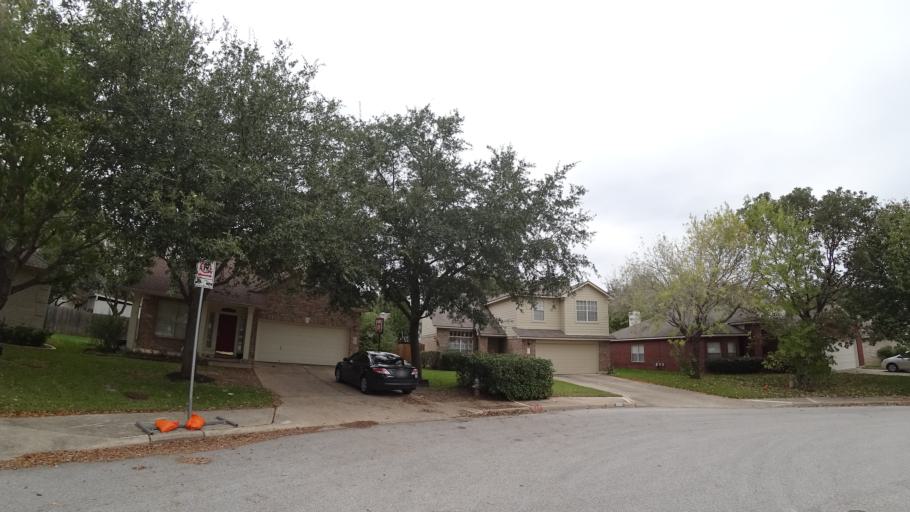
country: US
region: Texas
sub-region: Travis County
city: Shady Hollow
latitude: 30.1498
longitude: -97.8542
